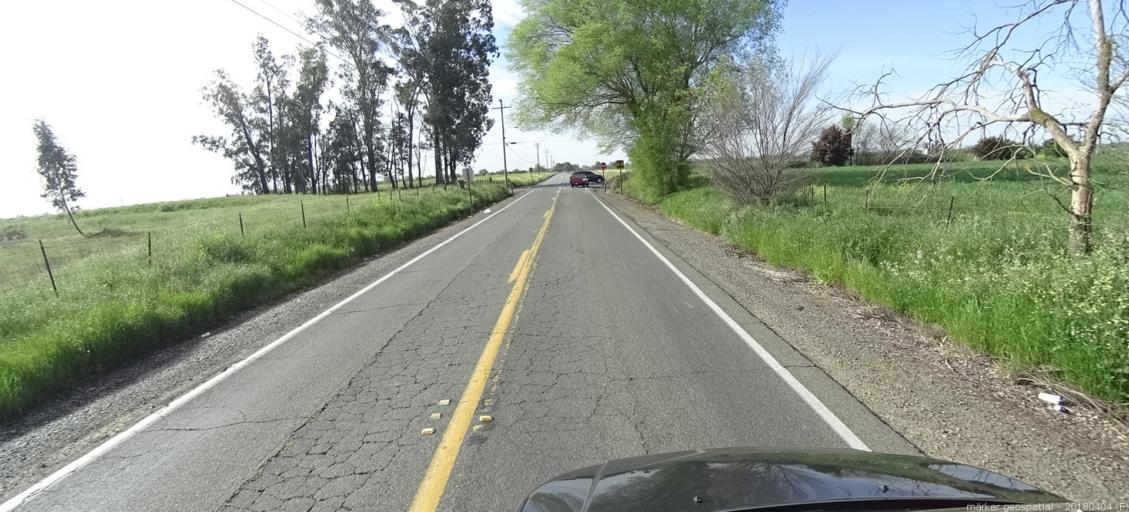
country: US
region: California
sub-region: Sacramento County
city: Herald
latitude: 38.2639
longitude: -121.2267
